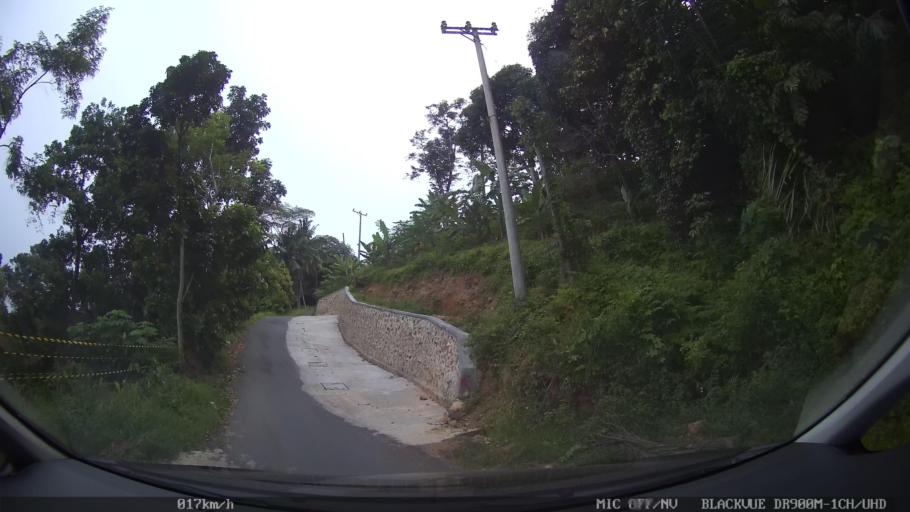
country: ID
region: Lampung
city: Bandarlampung
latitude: -5.4268
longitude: 105.3030
